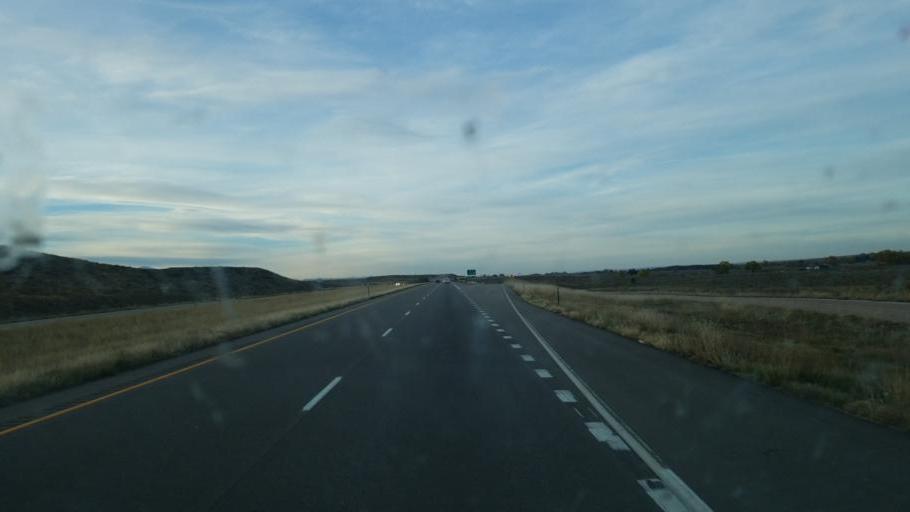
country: US
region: Colorado
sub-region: Pueblo County
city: Pueblo West
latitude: 38.4822
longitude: -104.6180
